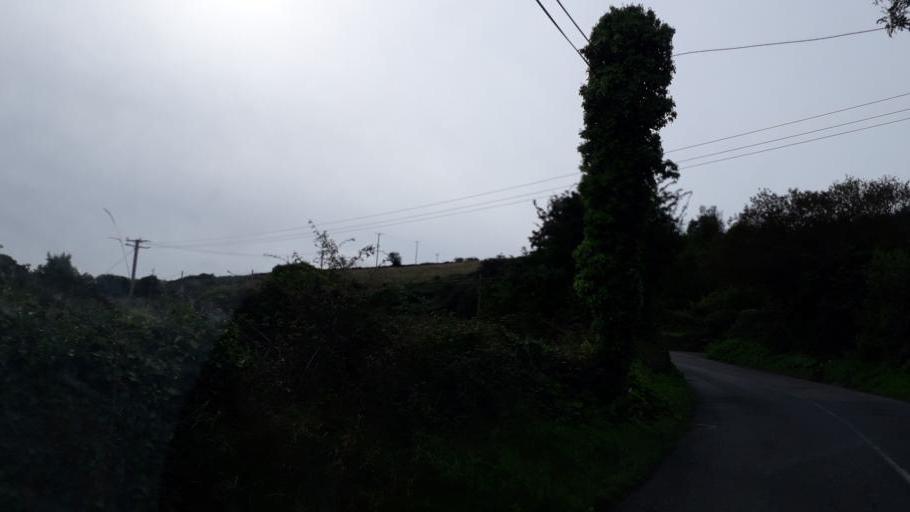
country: IE
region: Leinster
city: Foxrock
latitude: 53.2278
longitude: -6.2047
